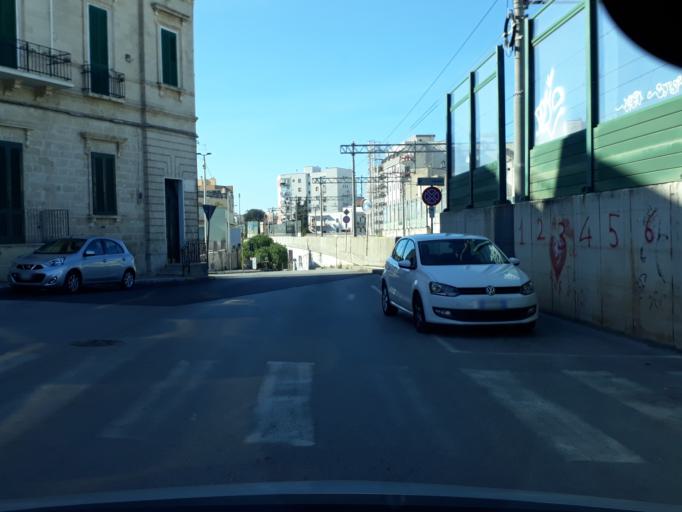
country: IT
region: Apulia
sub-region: Provincia di Bari
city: Monopoli
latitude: 40.9492
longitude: 17.2978
